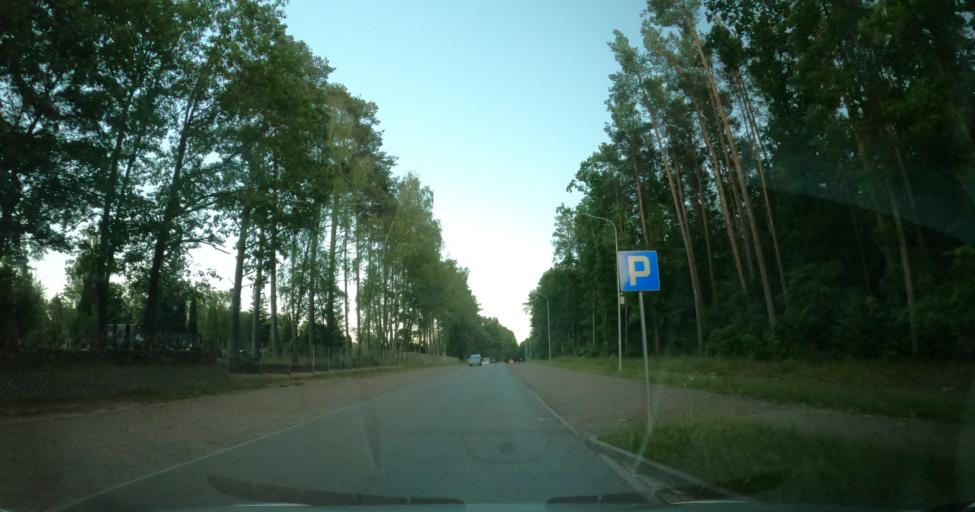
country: PL
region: Pomeranian Voivodeship
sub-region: Powiat leborski
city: Lebork
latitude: 54.5250
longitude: 17.7757
